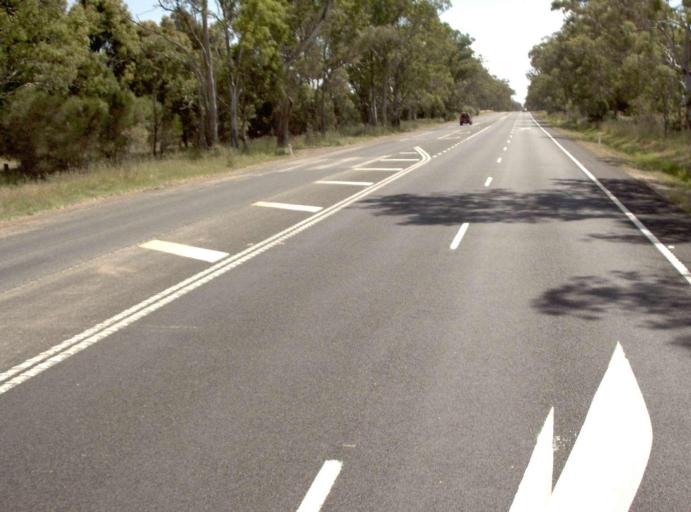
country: AU
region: Victoria
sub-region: Wellington
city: Sale
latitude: -37.9306
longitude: 147.1973
